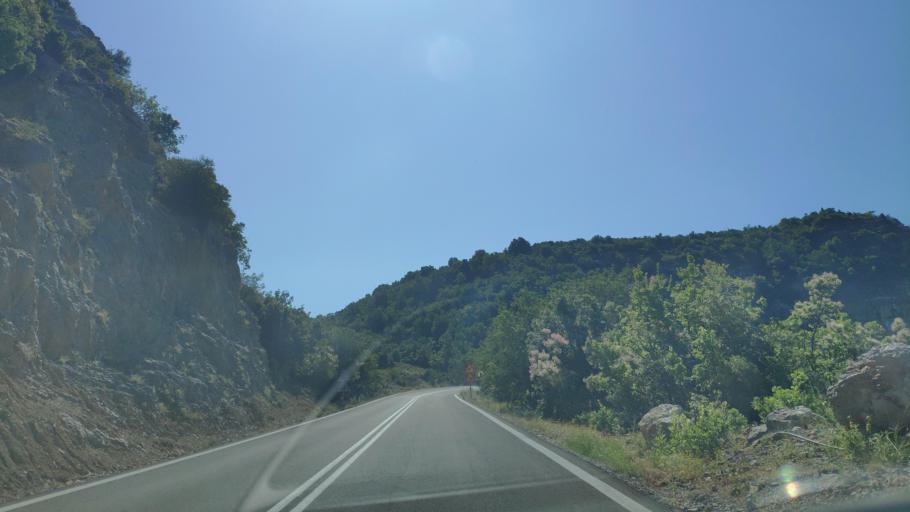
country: GR
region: West Greece
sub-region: Nomos Aitolias kai Akarnanias
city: Sardinia
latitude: 38.9250
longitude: 21.4185
